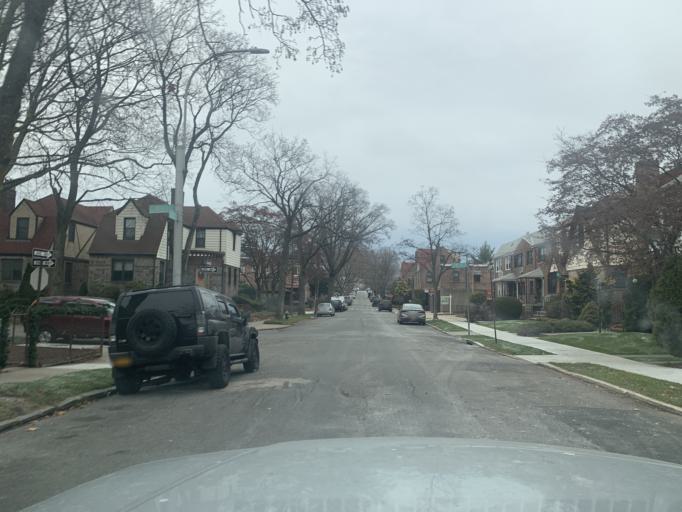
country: US
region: New York
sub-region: Queens County
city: Borough of Queens
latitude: 40.7197
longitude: -73.8716
